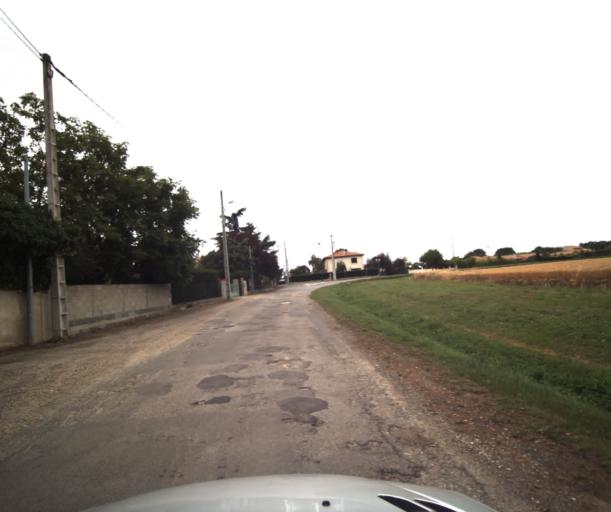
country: FR
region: Midi-Pyrenees
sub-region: Departement de la Haute-Garonne
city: Labarthe-sur-Leze
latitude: 43.4572
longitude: 1.4066
